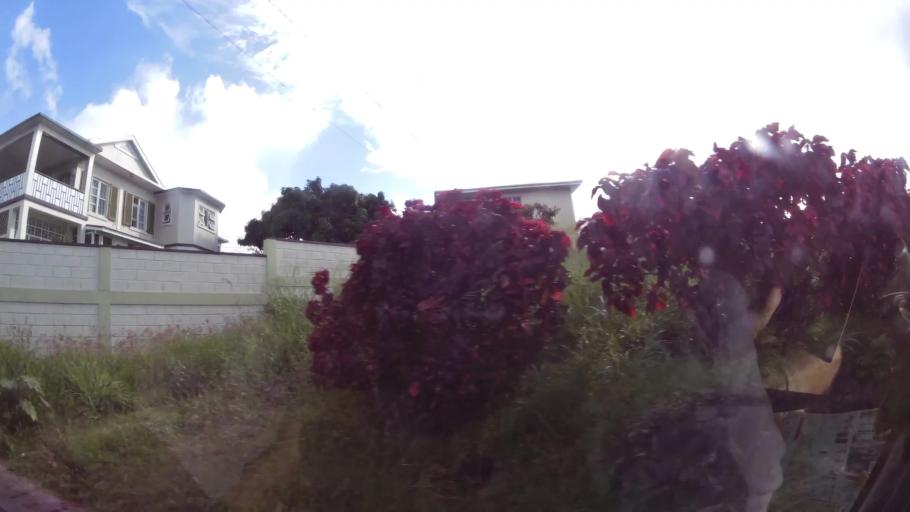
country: DM
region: Saint George
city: Roseau
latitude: 15.3055
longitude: -61.3803
